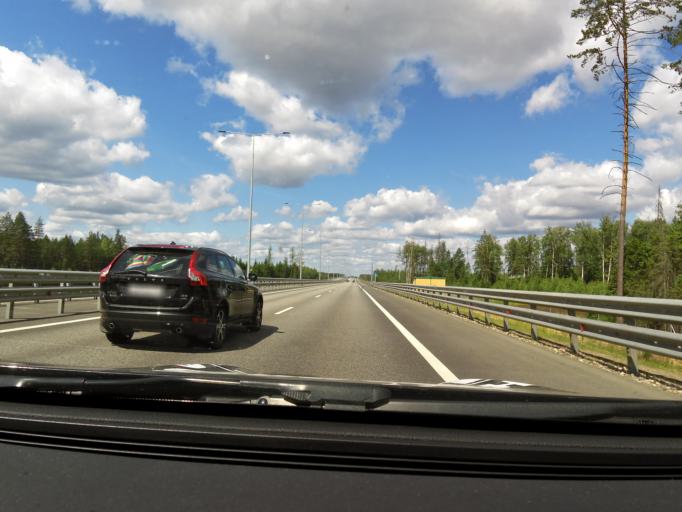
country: RU
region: Tverskaya
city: Krasnomayskiy
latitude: 57.4622
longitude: 34.3796
